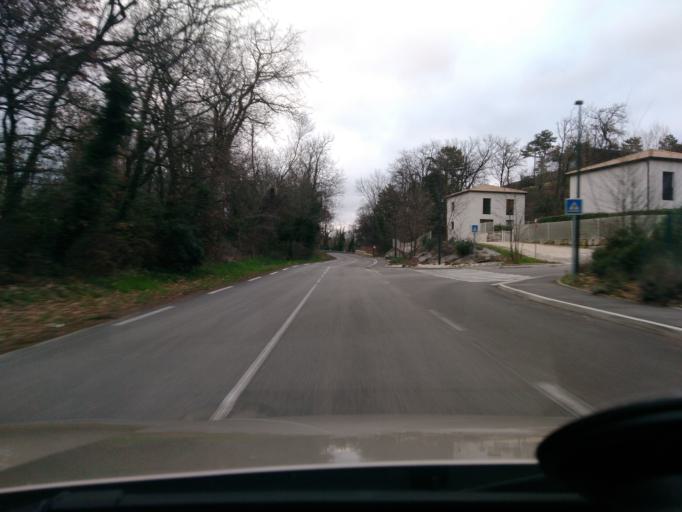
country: FR
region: Rhone-Alpes
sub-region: Departement de la Drome
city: Montelimar
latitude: 44.5595
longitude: 4.7703
